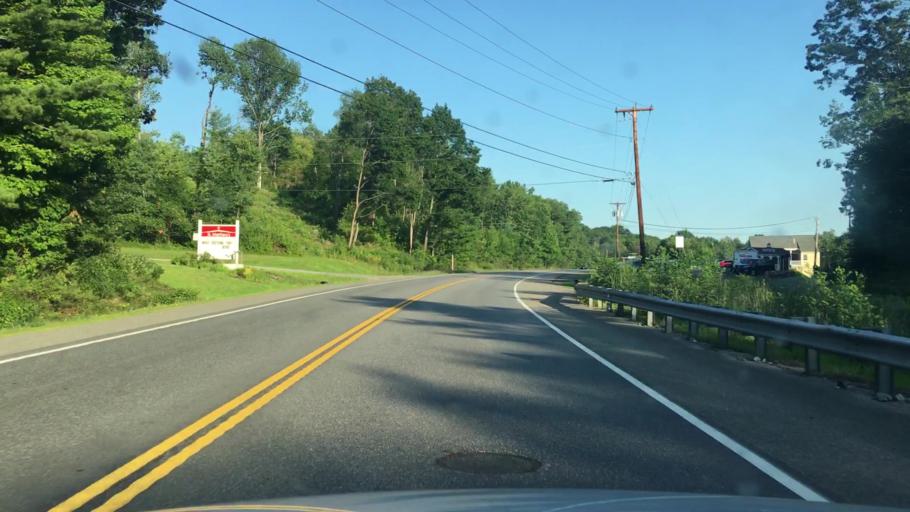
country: US
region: Maine
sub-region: Androscoggin County
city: Lisbon
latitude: 44.0107
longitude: -70.0853
